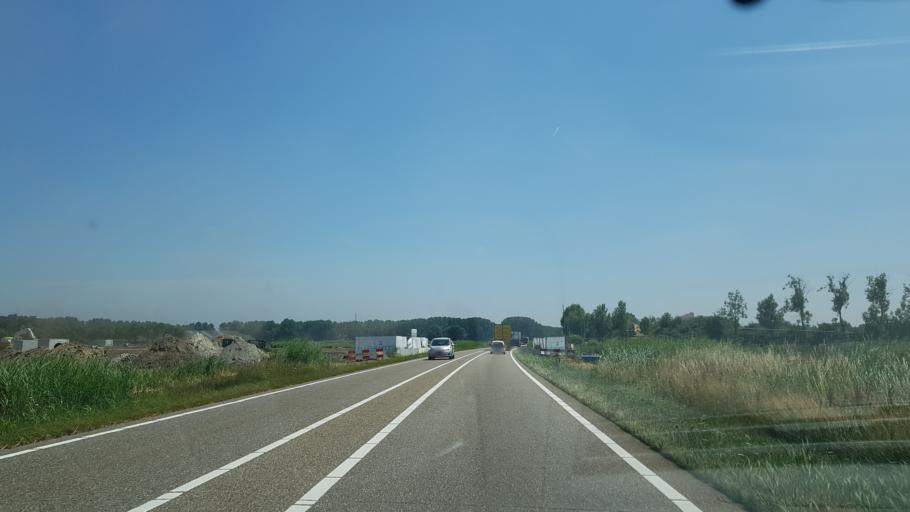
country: NL
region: North Brabant
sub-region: Gemeente Laarbeek
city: Aarle-Rixtel
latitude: 51.5502
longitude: 5.6350
